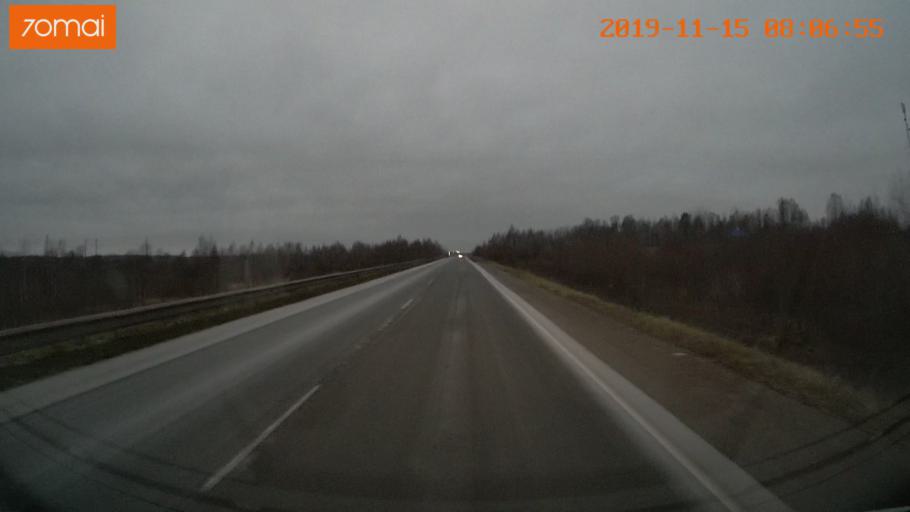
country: RU
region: Vologda
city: Cherepovets
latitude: 59.0244
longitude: 38.0275
